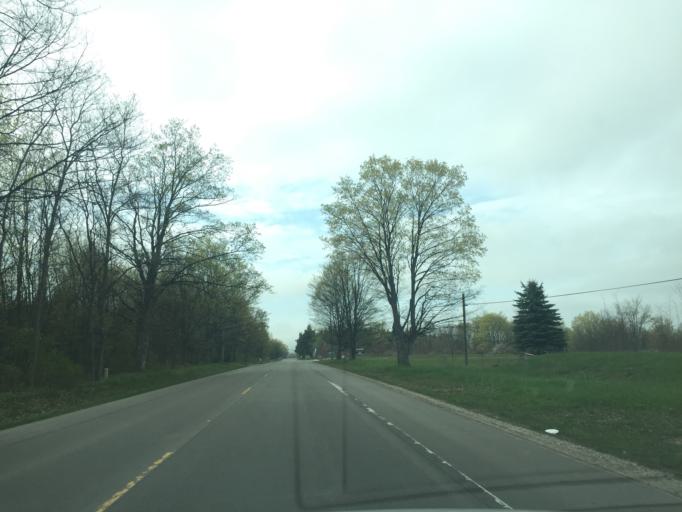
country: US
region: Michigan
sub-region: Leelanau County
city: Leland
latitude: 45.0755
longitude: -85.5901
